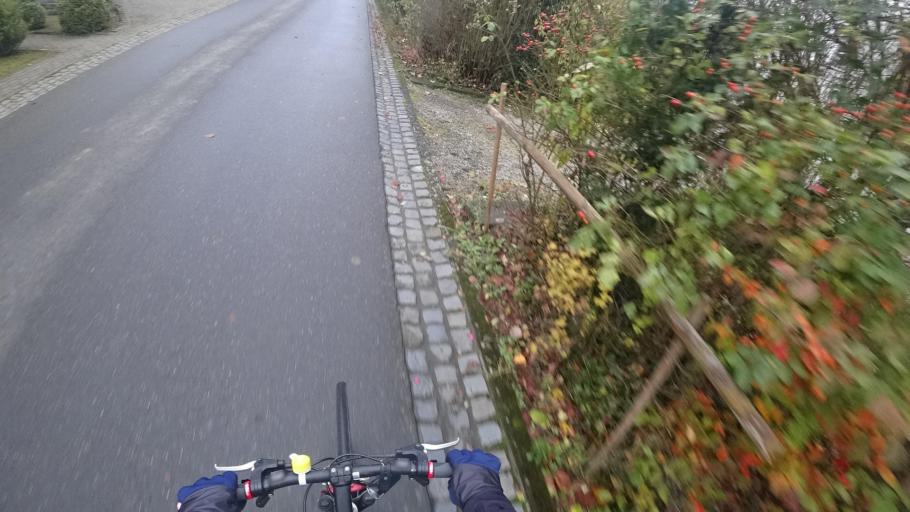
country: DE
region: Rheinland-Pfalz
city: Ney
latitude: 50.1829
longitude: 7.5371
